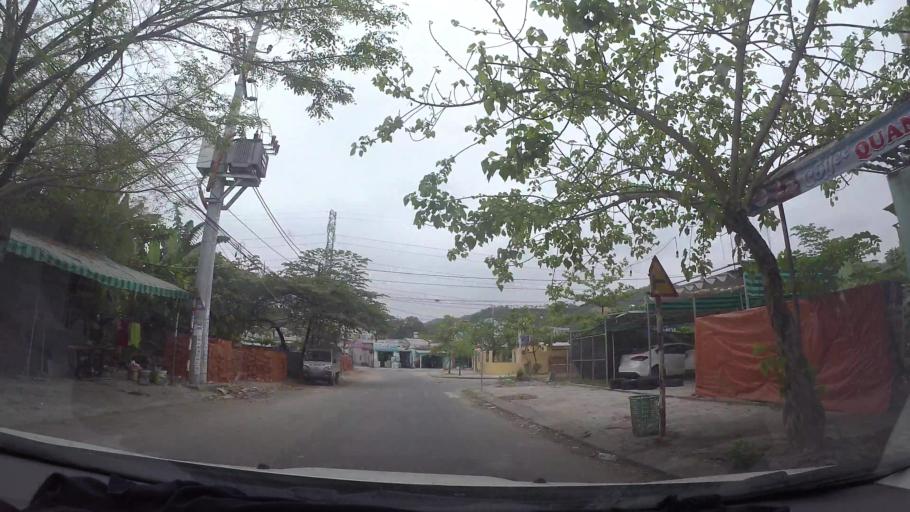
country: VN
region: Da Nang
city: Lien Chieu
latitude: 16.0695
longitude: 108.1455
